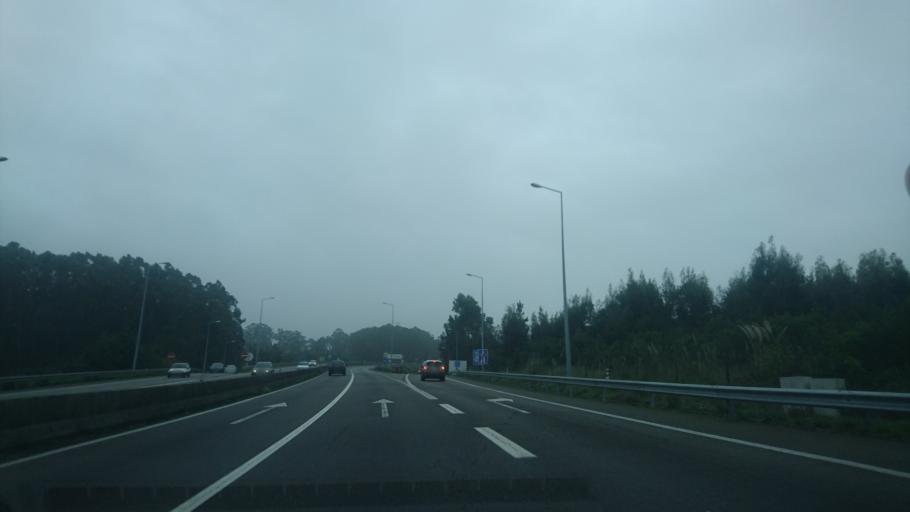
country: PT
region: Porto
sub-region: Vila Nova de Gaia
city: Gulpilhares
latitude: 41.0894
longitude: -8.6309
